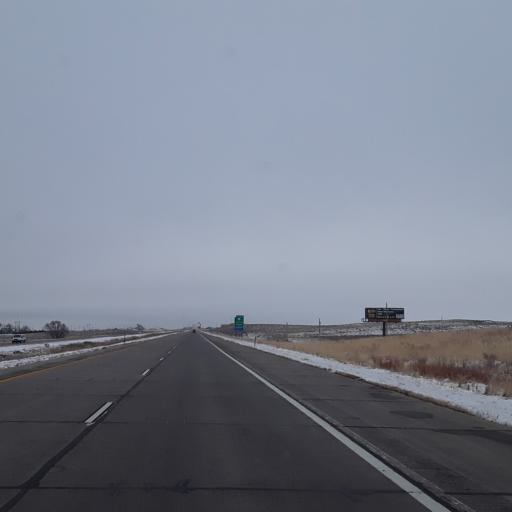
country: US
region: Colorado
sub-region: Logan County
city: Sterling
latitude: 40.6020
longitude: -103.1835
